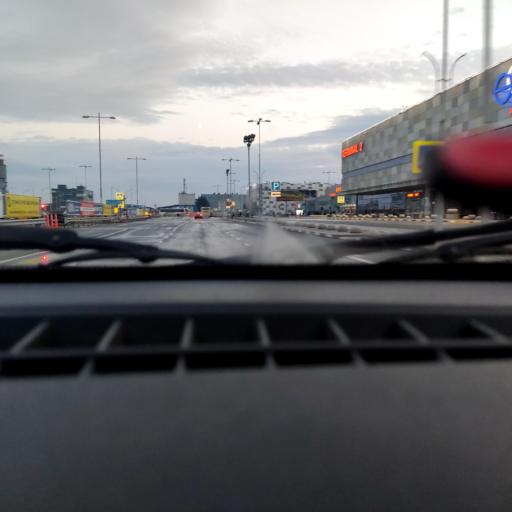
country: RU
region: Bashkortostan
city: Avdon
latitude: 54.5669
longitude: 55.8837
